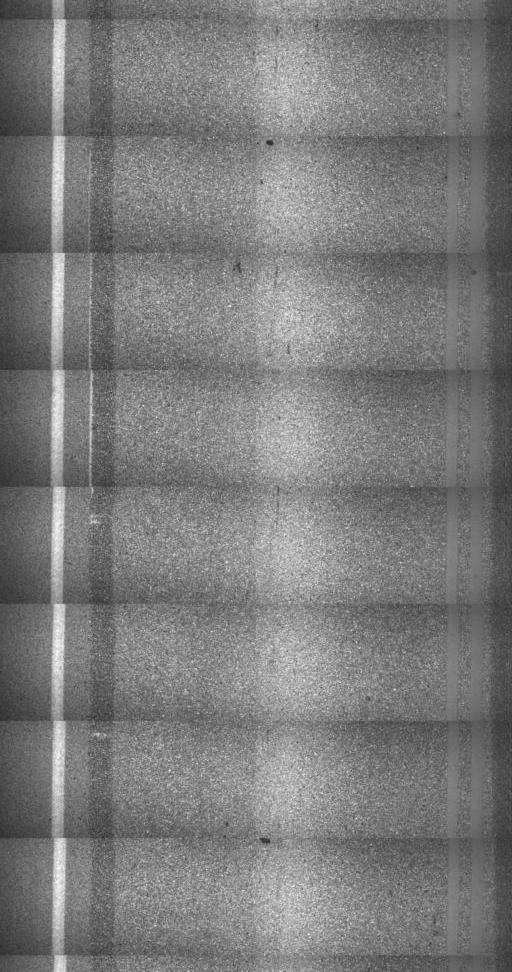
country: US
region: Vermont
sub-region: Lamoille County
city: Johnson
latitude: 44.6400
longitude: -72.6563
